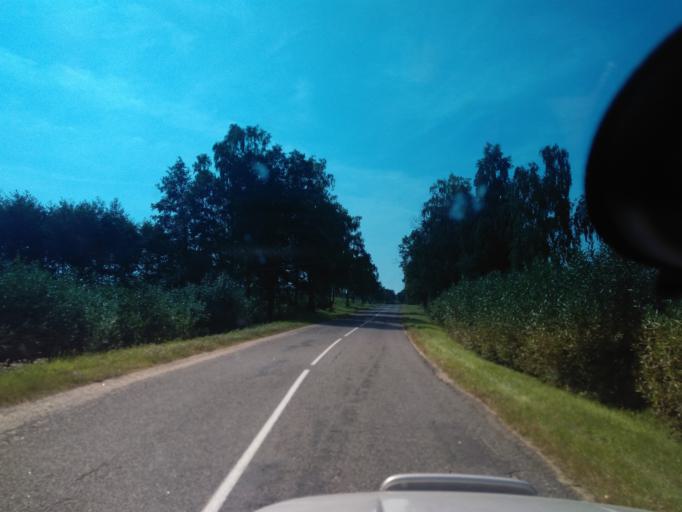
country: BY
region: Minsk
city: Kapyl'
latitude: 53.2295
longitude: 27.1692
